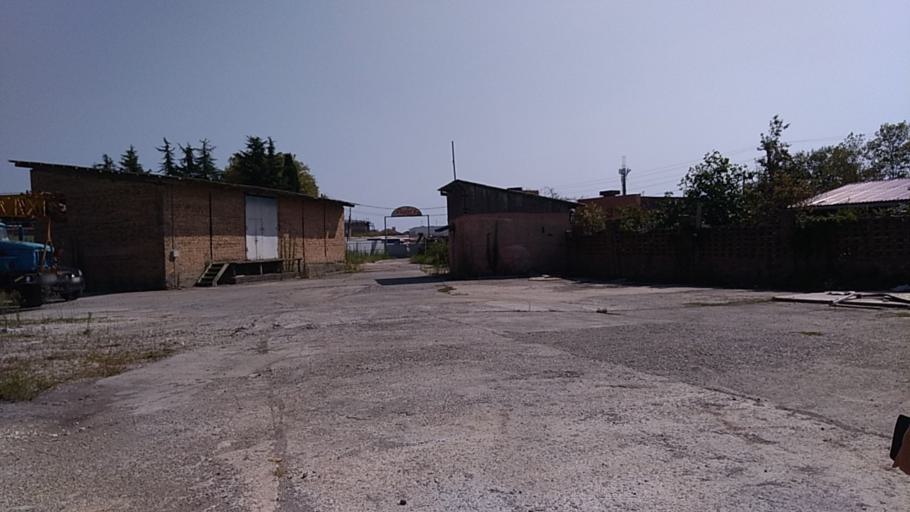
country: RU
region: Krasnodarskiy
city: Vysokoye
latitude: 43.4007
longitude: 39.9933
